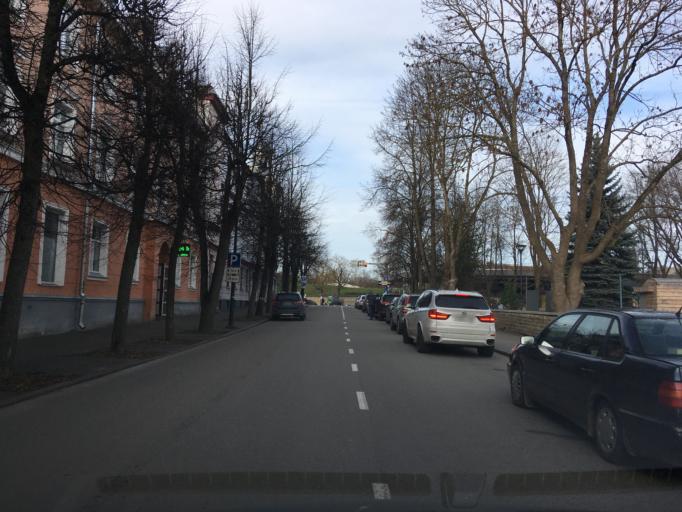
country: EE
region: Ida-Virumaa
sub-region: Narva linn
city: Narva
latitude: 59.3751
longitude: 28.1971
